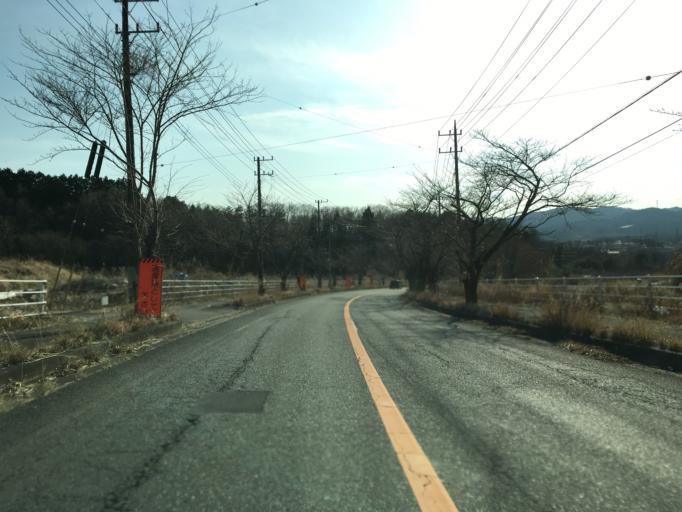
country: JP
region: Ibaraki
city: Takahagi
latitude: 36.7514
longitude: 140.7057
